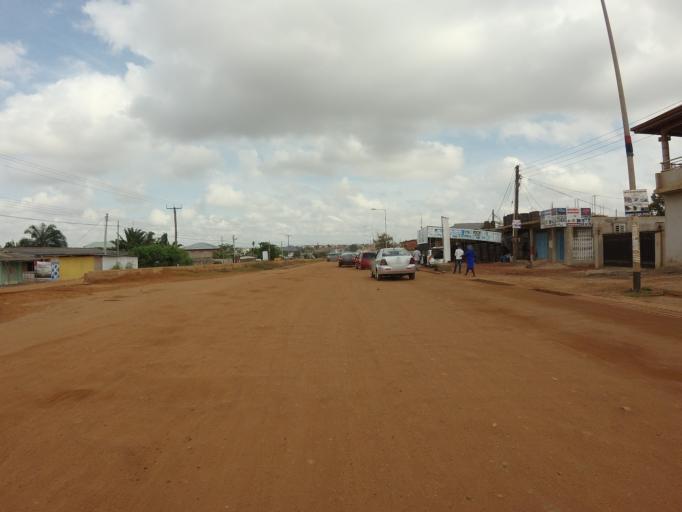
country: GH
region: Greater Accra
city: Teshi Old Town
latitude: 5.5985
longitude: -0.1190
